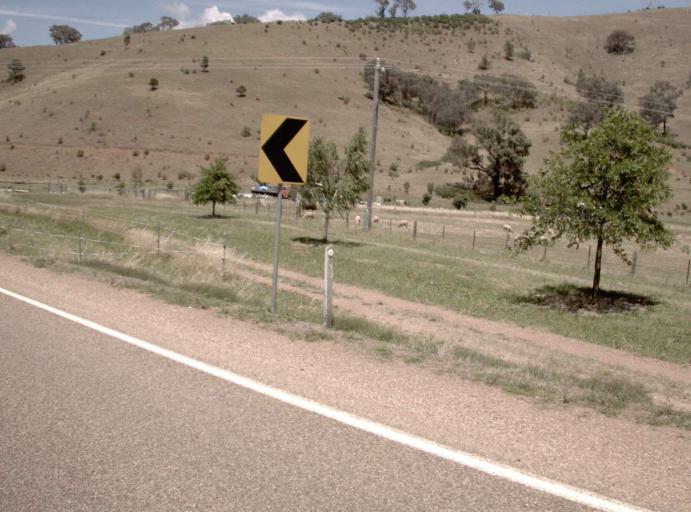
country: AU
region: Victoria
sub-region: East Gippsland
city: Bairnsdale
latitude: -37.2565
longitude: 147.7113
